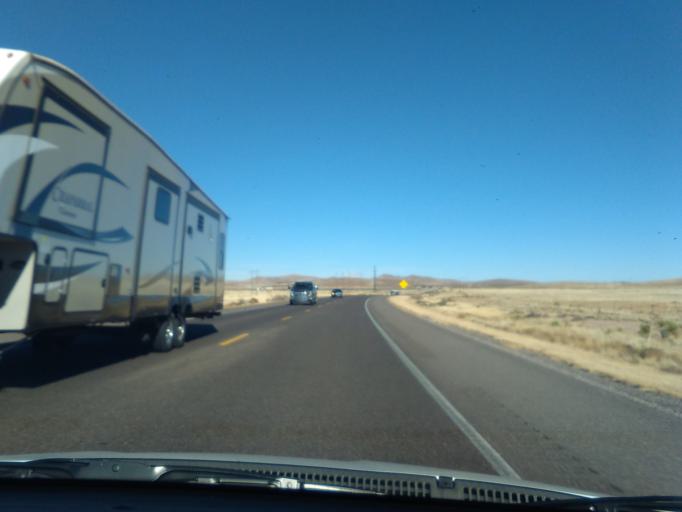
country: US
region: New Mexico
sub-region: Dona Ana County
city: Hatch
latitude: 32.5599
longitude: -107.4707
